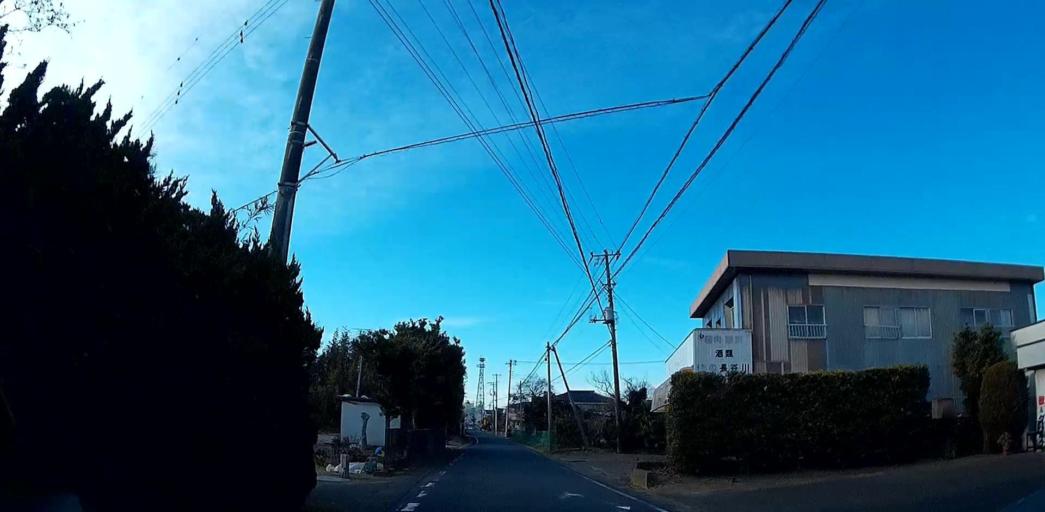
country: JP
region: Chiba
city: Omigawa
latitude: 35.8394
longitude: 140.7136
